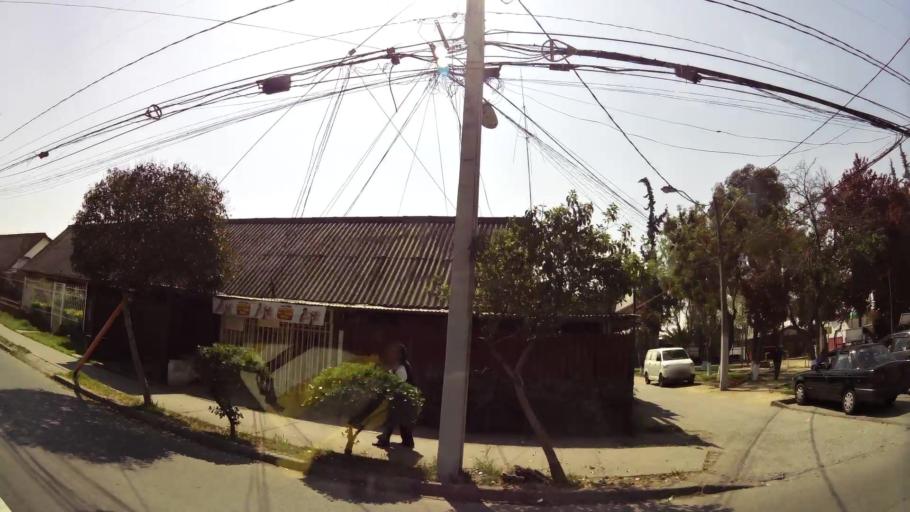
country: CL
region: Santiago Metropolitan
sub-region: Provincia de Santiago
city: La Pintana
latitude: -33.5506
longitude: -70.6096
